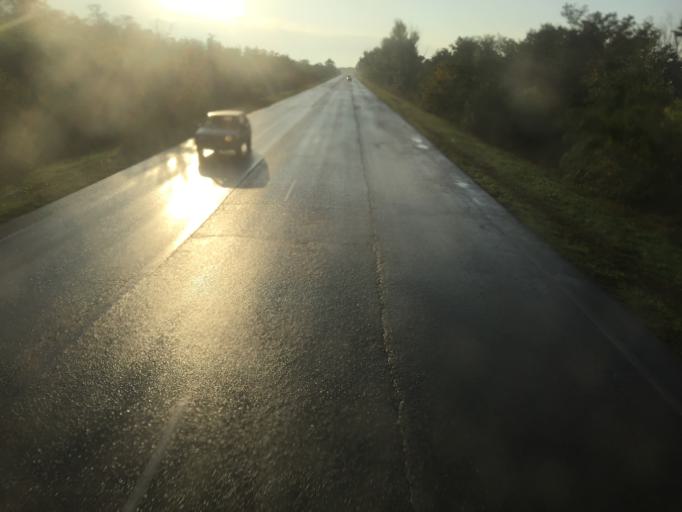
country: RU
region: Rostov
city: Kirovskaya
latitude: 47.0213
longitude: 39.8979
